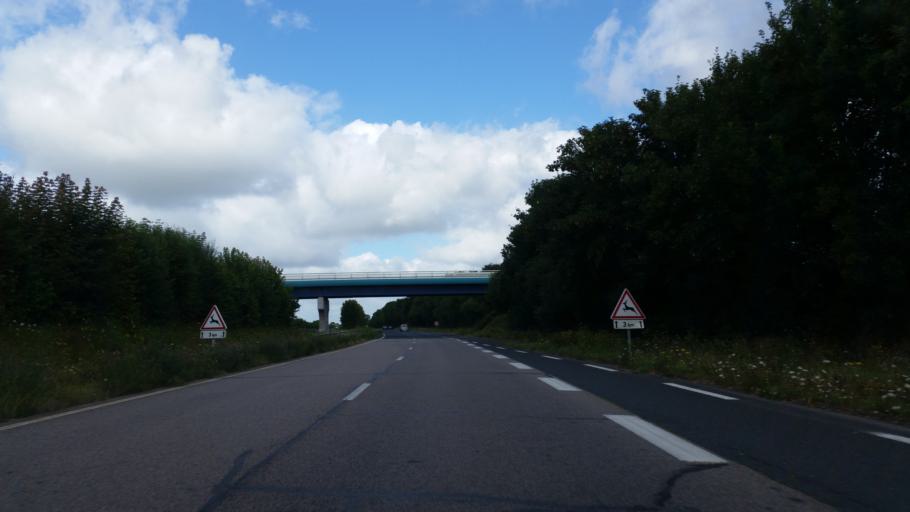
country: FR
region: Lower Normandy
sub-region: Departement du Calvados
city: Le Molay-Littry
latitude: 49.3365
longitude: -0.9233
